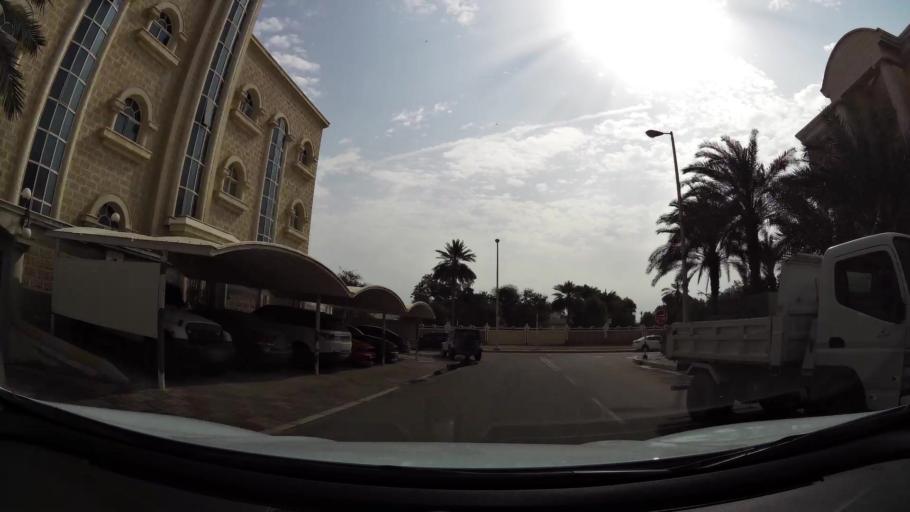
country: AE
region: Abu Dhabi
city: Abu Dhabi
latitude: 24.4381
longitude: 54.4188
